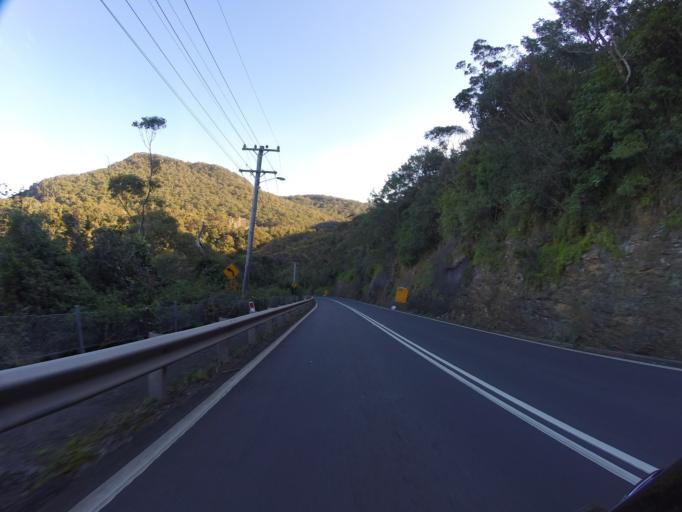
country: AU
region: New South Wales
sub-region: Wollongong
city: Helensburgh
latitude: -34.2440
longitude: 150.9749
